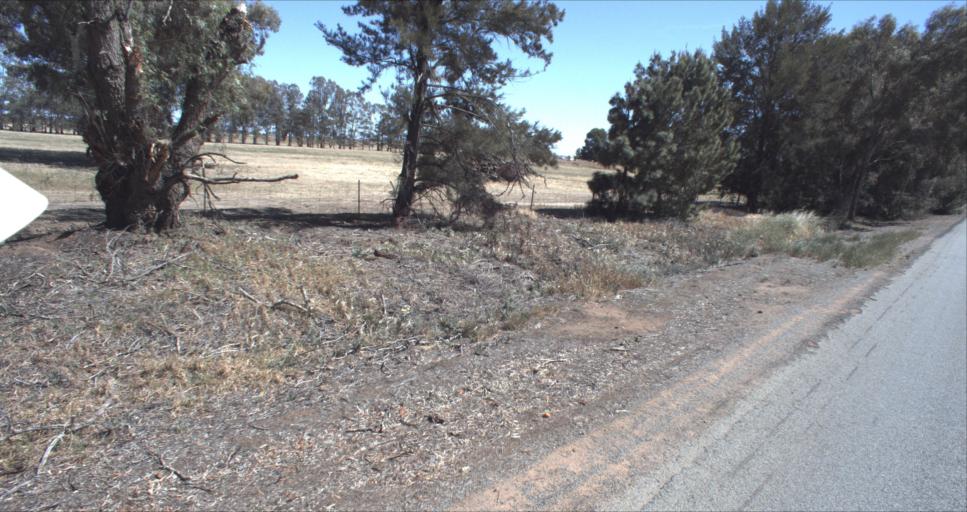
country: AU
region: New South Wales
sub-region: Leeton
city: Leeton
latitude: -34.5743
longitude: 146.3100
